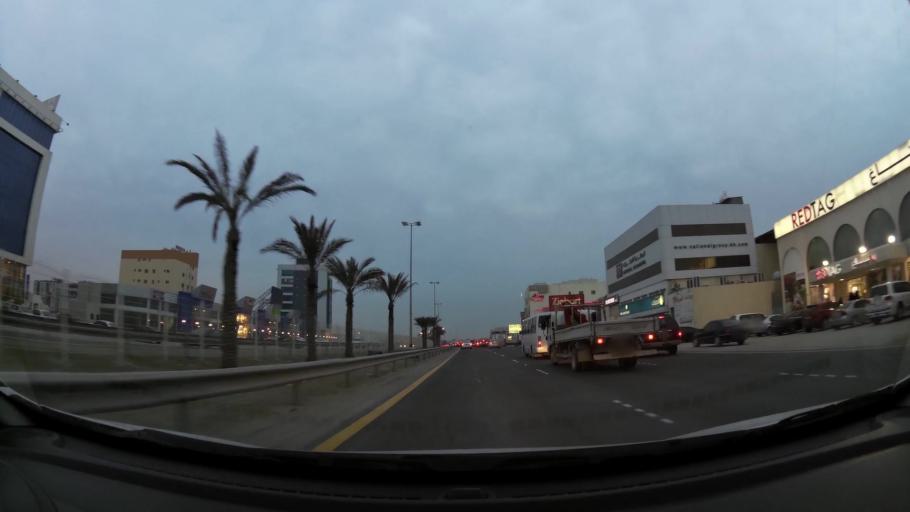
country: BH
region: Northern
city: Ar Rifa'
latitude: 26.1365
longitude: 50.5838
